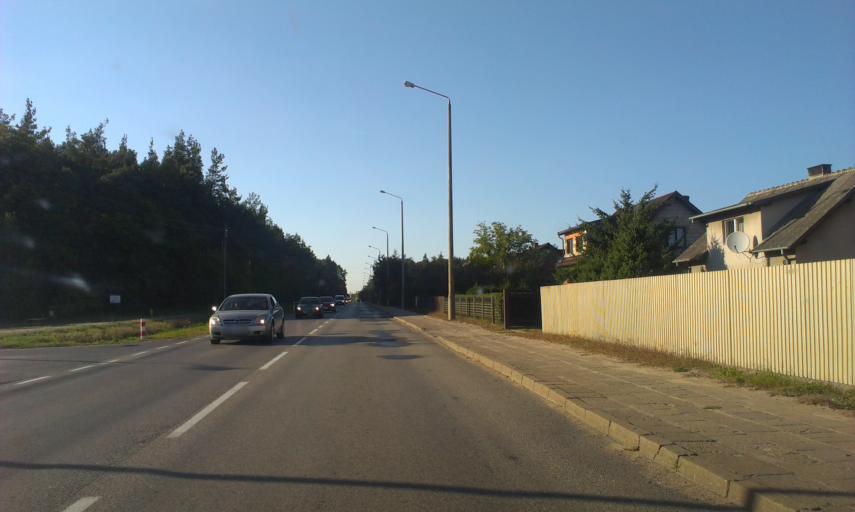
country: PL
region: Kujawsko-Pomorskie
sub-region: Powiat tucholski
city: Tuchola
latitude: 53.5705
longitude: 17.8891
